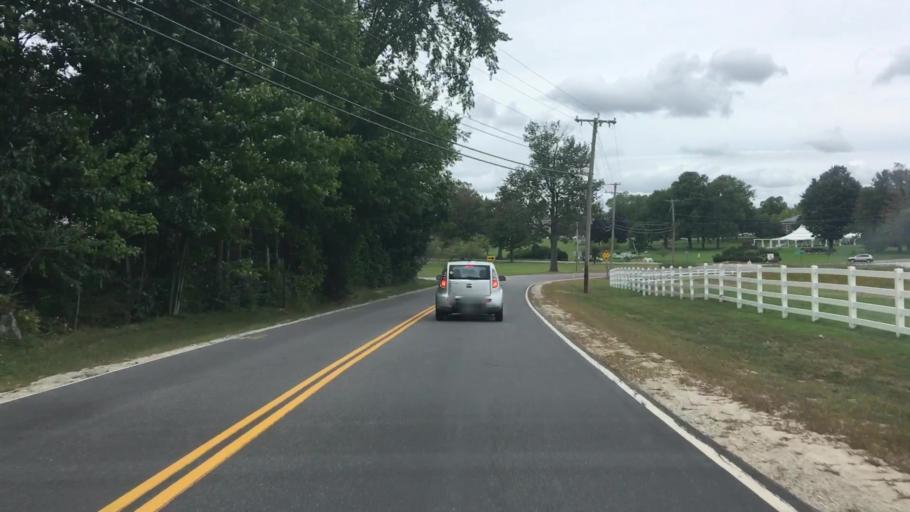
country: US
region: Maine
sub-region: Cumberland County
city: New Gloucester
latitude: 43.8984
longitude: -70.2565
